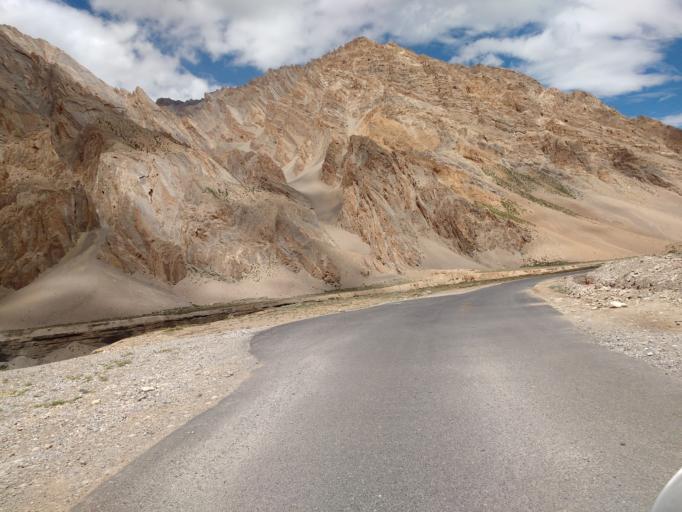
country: IN
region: Himachal Pradesh
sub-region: Lahul and Spiti
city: Kyelang
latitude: 33.0270
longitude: 77.5896
